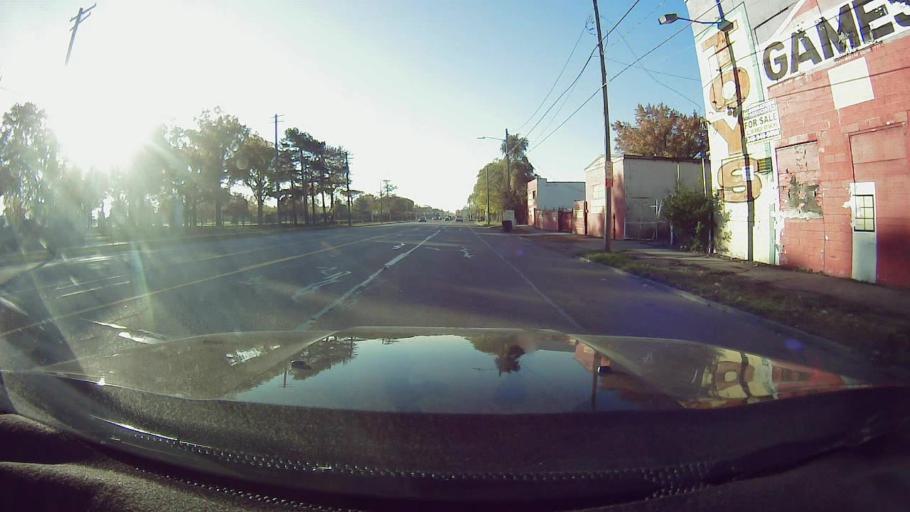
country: US
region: Michigan
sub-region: Wayne County
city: Hamtramck
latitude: 42.4224
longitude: -83.0239
